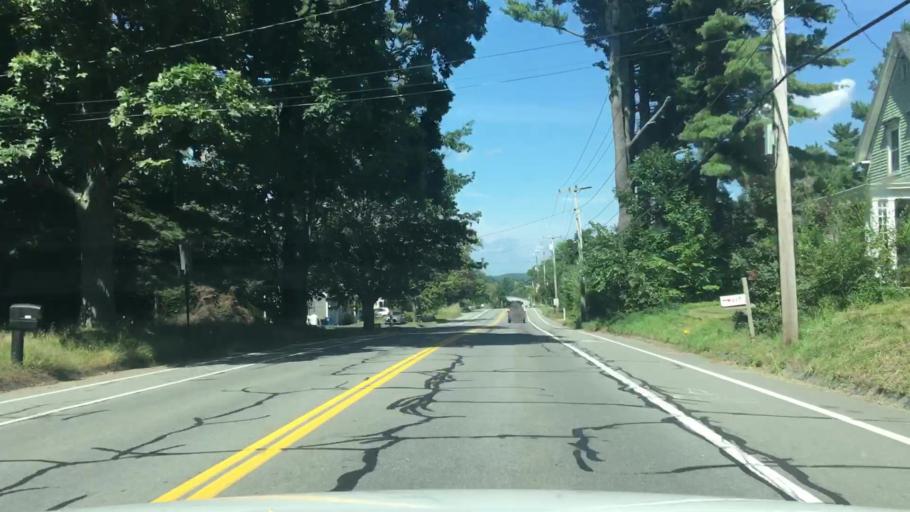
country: US
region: Maine
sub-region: Cumberland County
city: Falmouth
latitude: 43.7229
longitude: -70.2939
